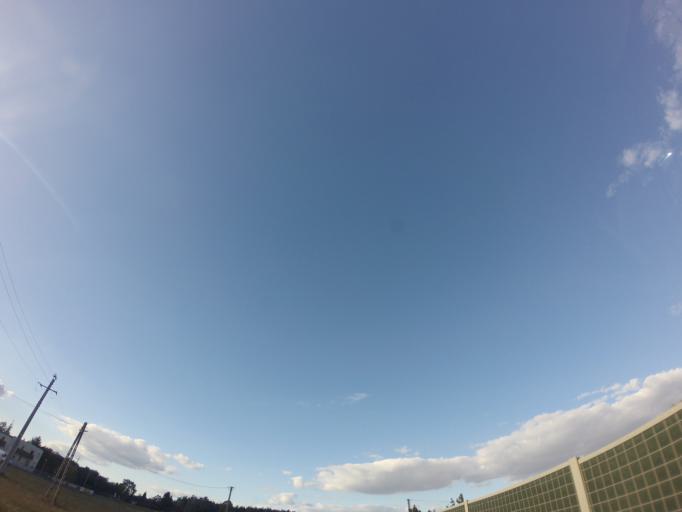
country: PL
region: Greater Poland Voivodeship
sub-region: Powiat nowotomyski
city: Nowy Tomysl
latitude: 52.3110
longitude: 16.1112
